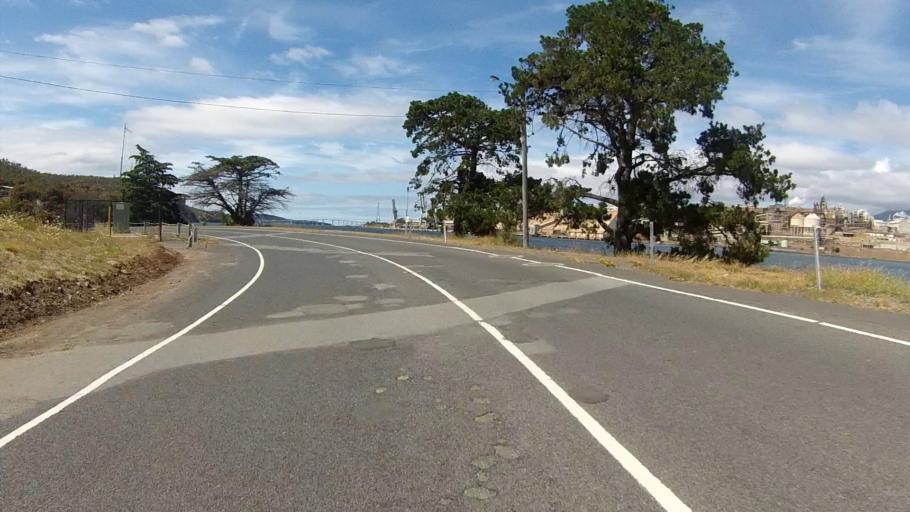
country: AU
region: Tasmania
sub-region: Glenorchy
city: Lutana
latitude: -42.8244
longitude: 147.3173
